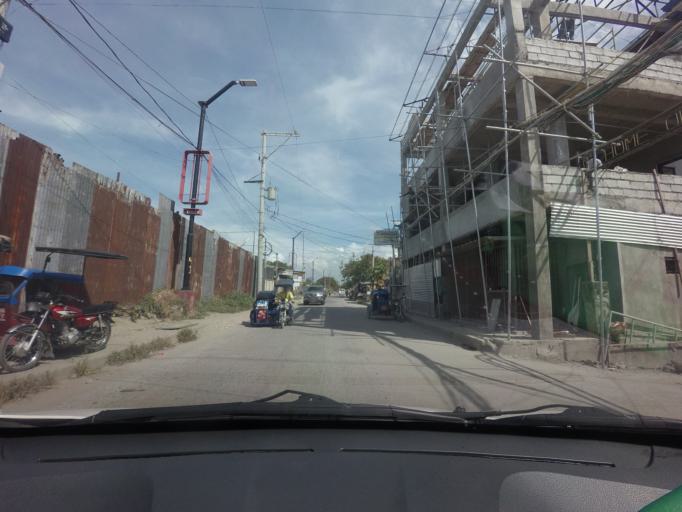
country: PH
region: Calabarzon
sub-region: Province of Rizal
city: Taguig
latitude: 14.5275
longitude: 121.0883
